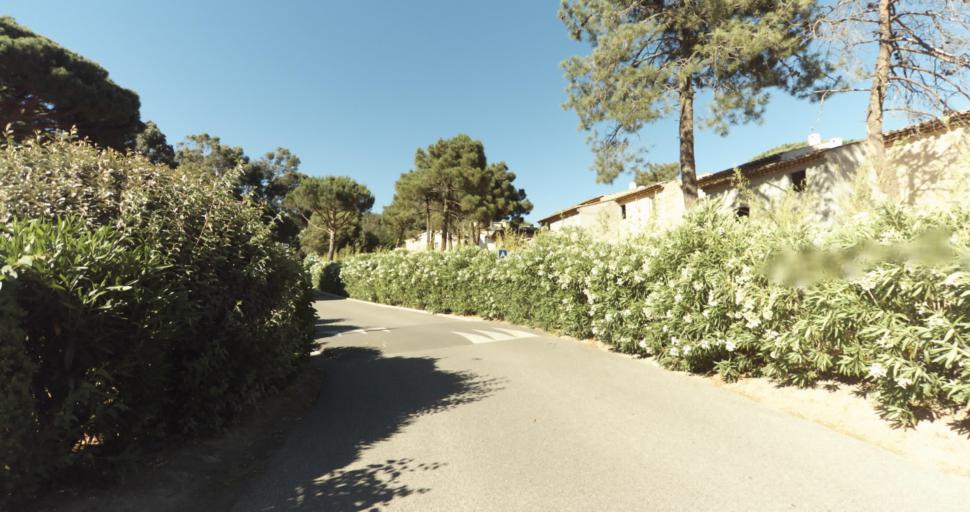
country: FR
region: Provence-Alpes-Cote d'Azur
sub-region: Departement du Var
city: Gassin
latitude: 43.2539
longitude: 6.6009
